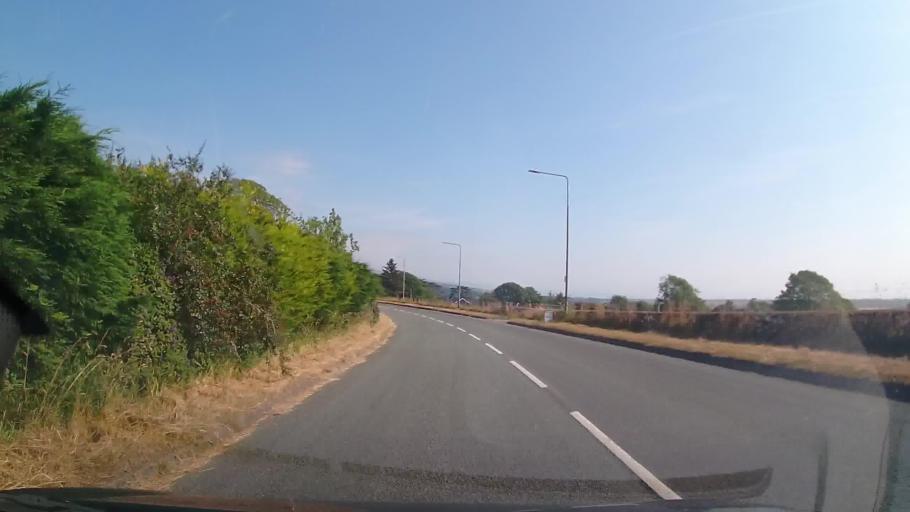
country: GB
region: Wales
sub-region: Gwynedd
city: Llanfair
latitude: 52.8403
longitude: -4.1149
